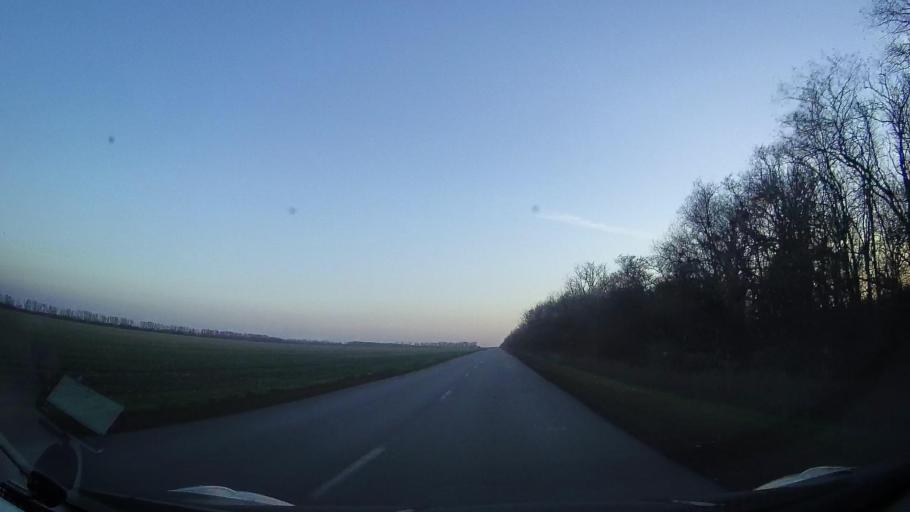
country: RU
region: Rostov
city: Zernograd
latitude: 47.0402
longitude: 40.3916
